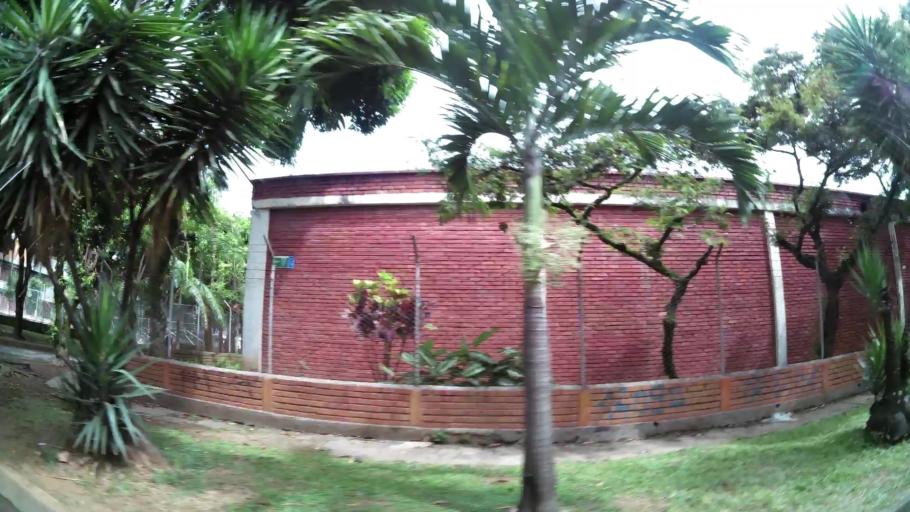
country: CO
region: Valle del Cauca
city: Cali
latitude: 3.3927
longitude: -76.5476
